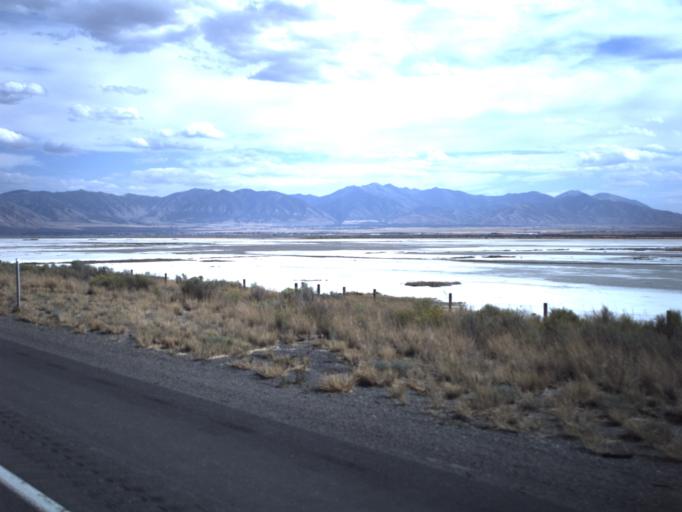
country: US
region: Utah
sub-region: Tooele County
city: Grantsville
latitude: 40.6818
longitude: -112.4299
